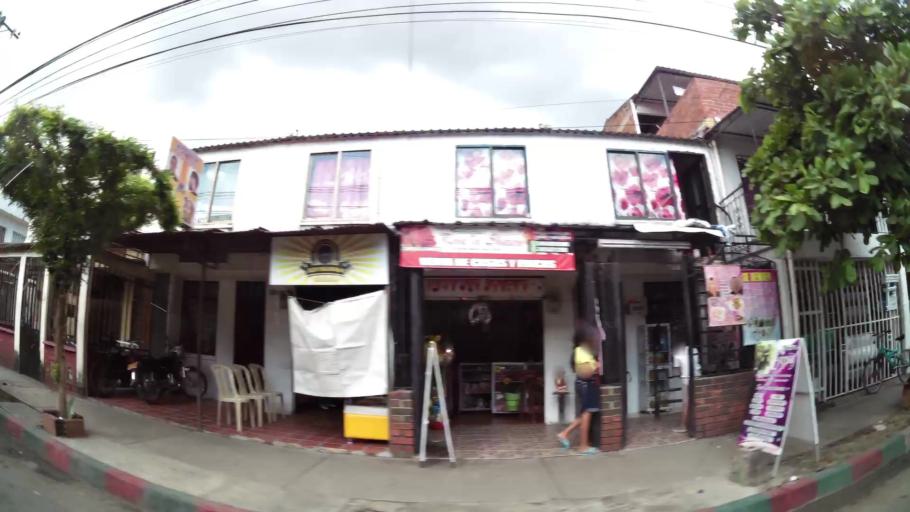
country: CO
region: Valle del Cauca
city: Cali
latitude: 3.3979
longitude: -76.5044
